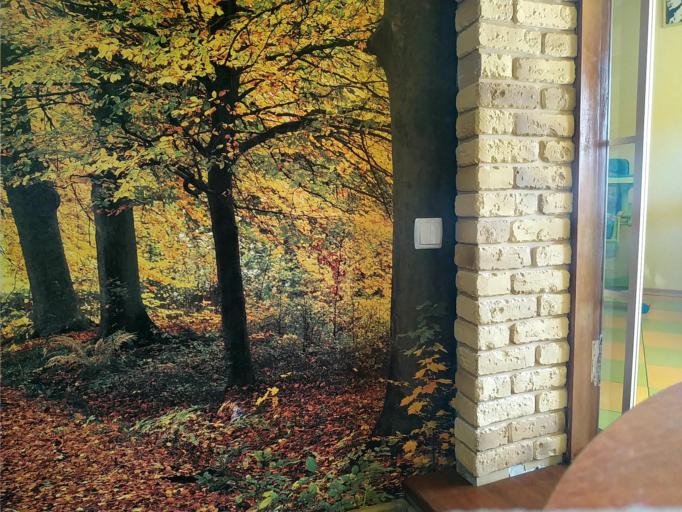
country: RU
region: Smolensk
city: Katyn'
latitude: 54.9798
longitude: 31.7299
